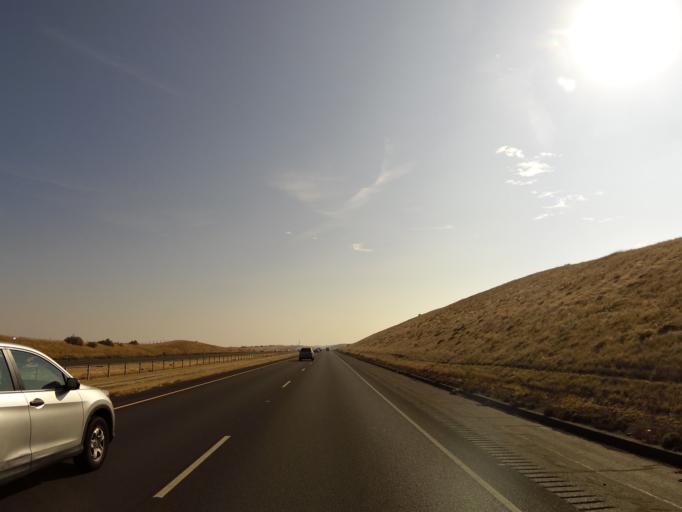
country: US
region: California
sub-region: Kings County
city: Avenal
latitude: 36.0434
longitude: -120.0466
